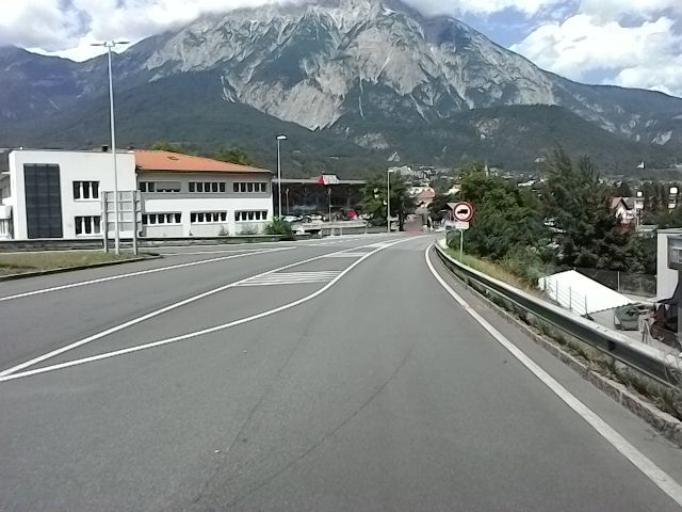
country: AT
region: Tyrol
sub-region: Politischer Bezirk Innsbruck Land
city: Telfs
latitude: 47.3028
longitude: 11.0704
